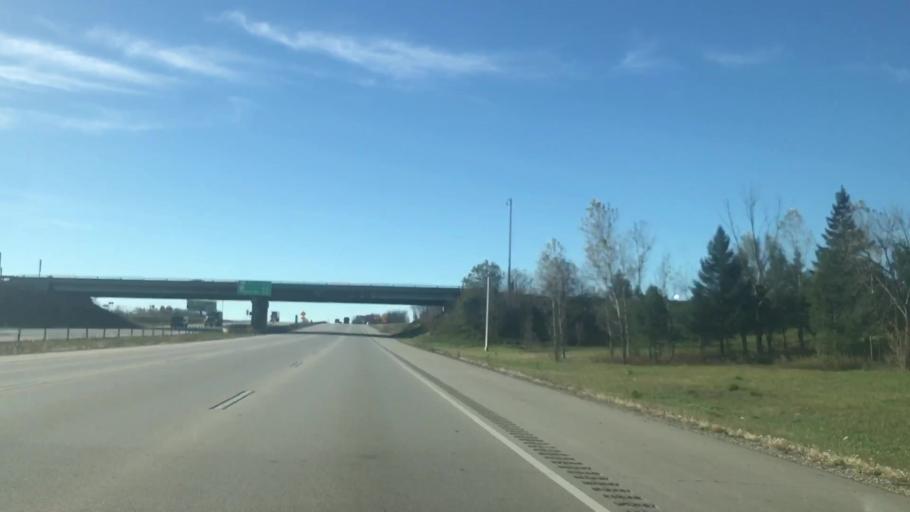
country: US
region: Wisconsin
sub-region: Washington County
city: Richfield
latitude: 43.2520
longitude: -88.1819
